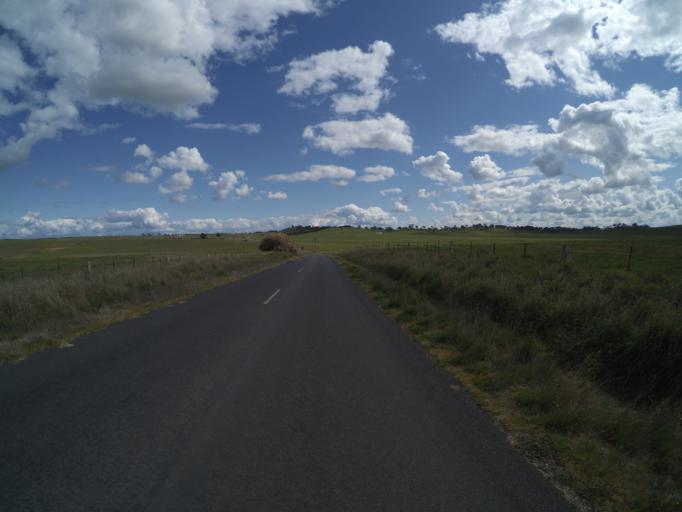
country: AU
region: New South Wales
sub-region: Yass Valley
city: Yass
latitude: -34.8763
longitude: 148.9024
